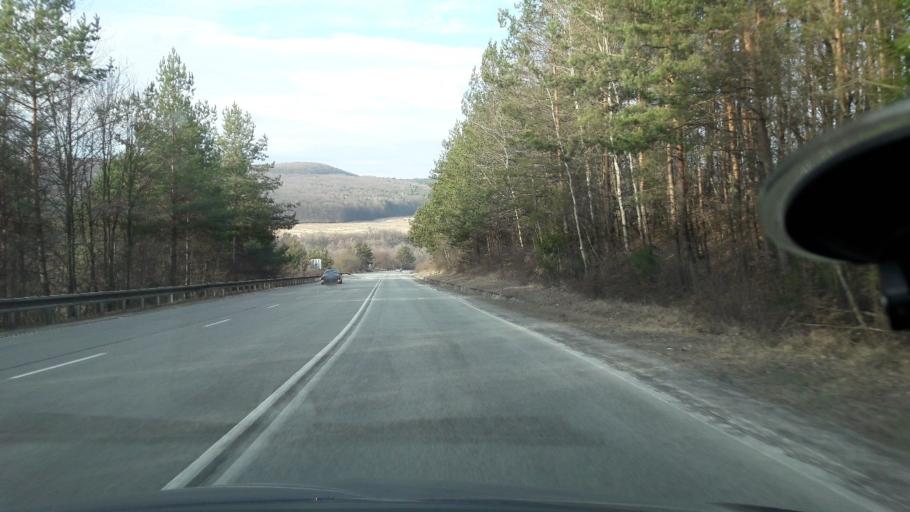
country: SK
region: Nitriansky
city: Prievidza
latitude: 48.7775
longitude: 18.6755
